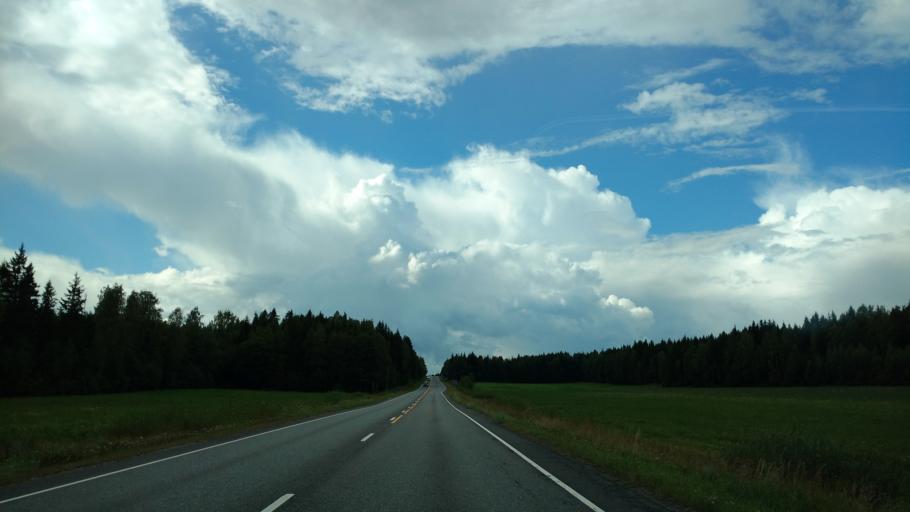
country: FI
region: Varsinais-Suomi
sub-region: Turku
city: Sauvo
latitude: 60.3985
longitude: 22.8421
